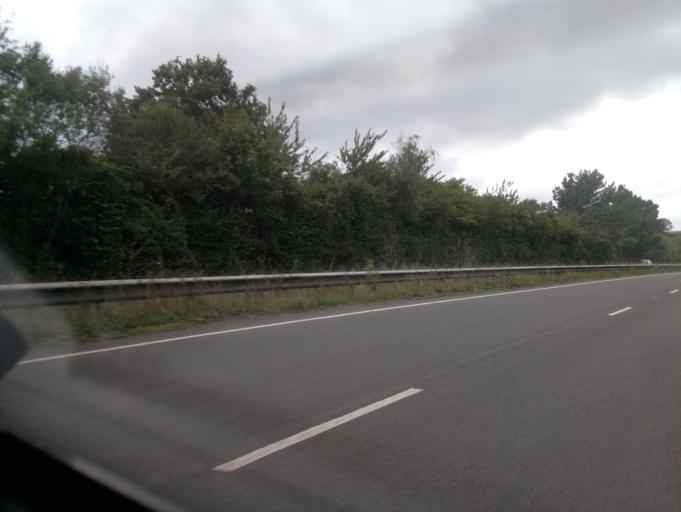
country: GB
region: England
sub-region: Devon
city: Marldon
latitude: 50.4603
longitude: -3.5903
